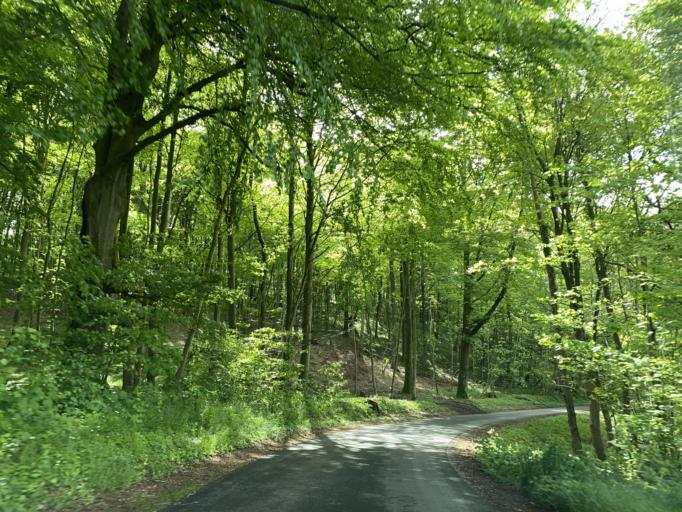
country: DK
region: South Denmark
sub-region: Aabenraa Kommune
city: Aabenraa
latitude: 55.0046
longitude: 9.4679
